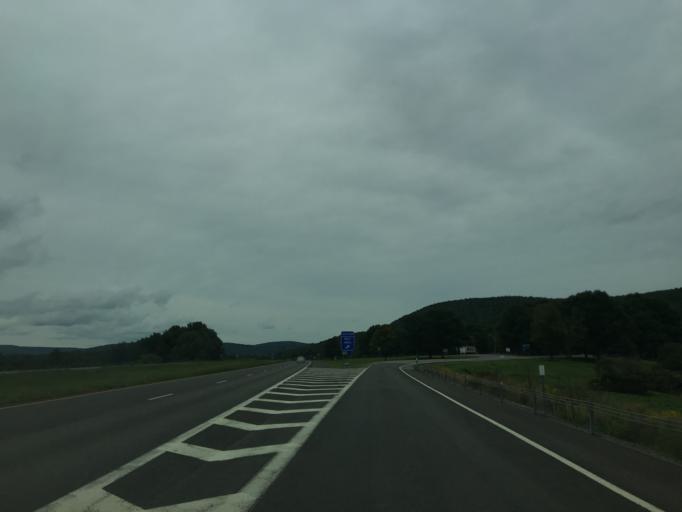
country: US
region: New York
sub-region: Otsego County
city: Unadilla
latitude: 42.3252
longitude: -75.2941
